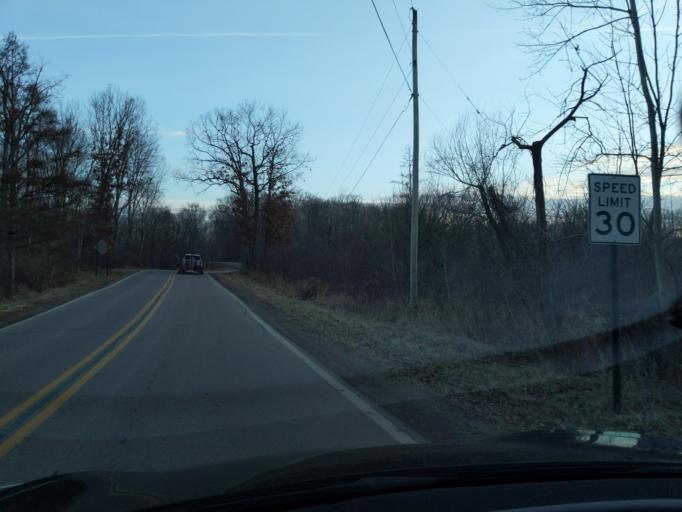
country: US
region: Michigan
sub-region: Oakland County
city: Milford
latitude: 42.6398
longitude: -83.7152
